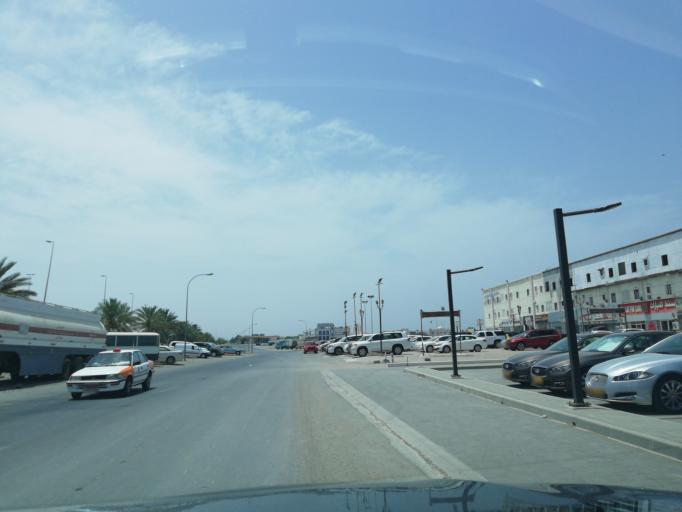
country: OM
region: Muhafazat Masqat
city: As Sib al Jadidah
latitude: 23.6561
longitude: 58.2034
